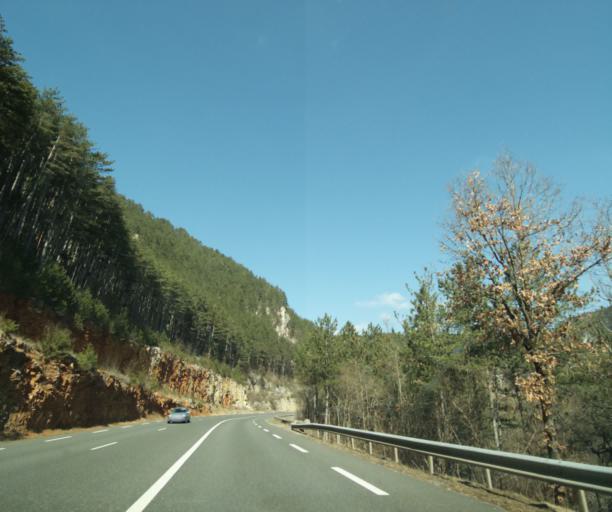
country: FR
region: Languedoc-Roussillon
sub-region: Departement de la Lozere
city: Mende
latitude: 44.4919
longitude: 3.4575
